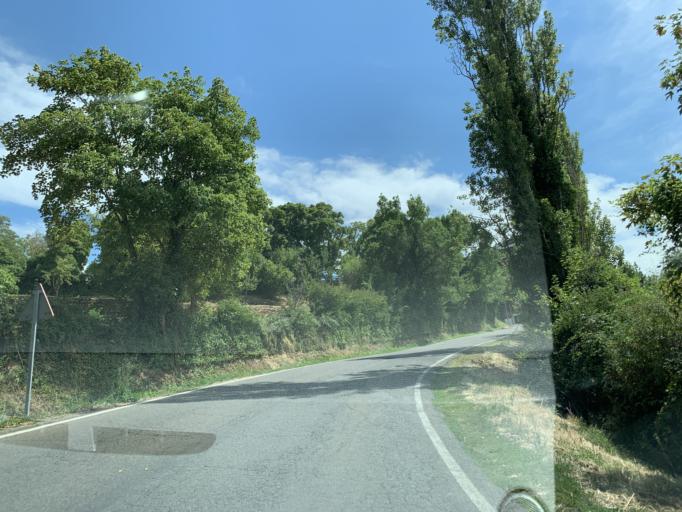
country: ES
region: Aragon
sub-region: Provincia de Huesca
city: Jaca
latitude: 42.5728
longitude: -0.5559
